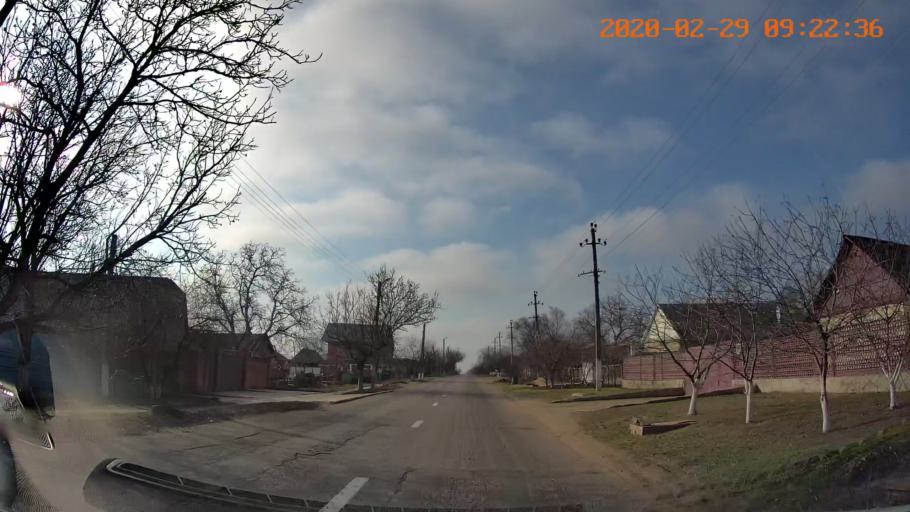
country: MD
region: Telenesti
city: Pervomaisc
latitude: 46.7338
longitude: 29.9636
